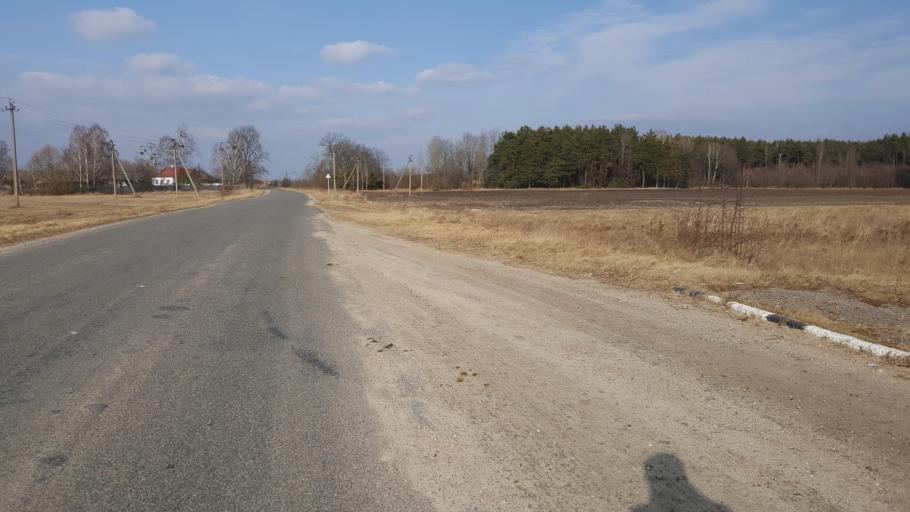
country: BY
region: Brest
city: Kamyanyets
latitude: 52.4157
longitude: 23.8877
